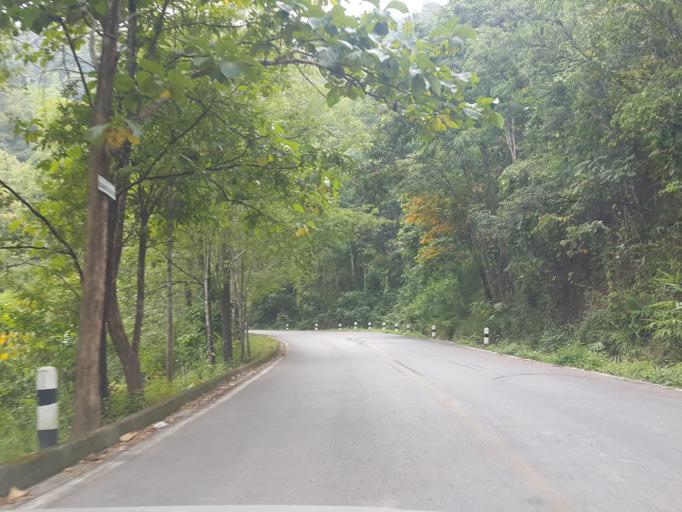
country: TH
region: Mae Hong Son
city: Mae Hi
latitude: 19.2708
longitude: 98.5019
